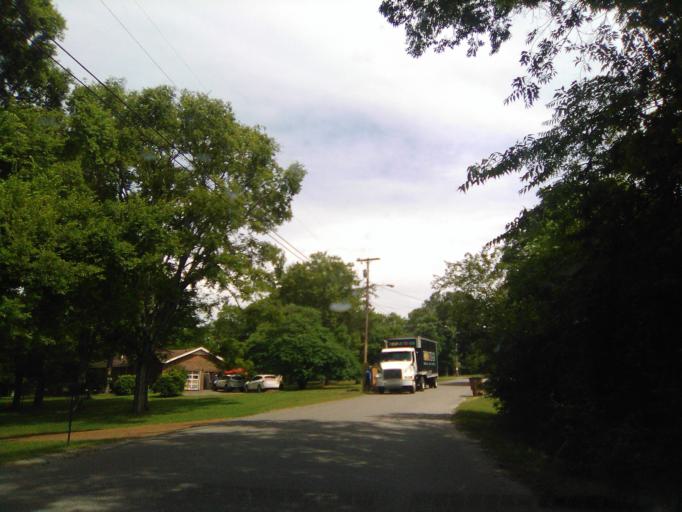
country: US
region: Tennessee
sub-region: Davidson County
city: Belle Meade
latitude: 36.1277
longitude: -86.8958
